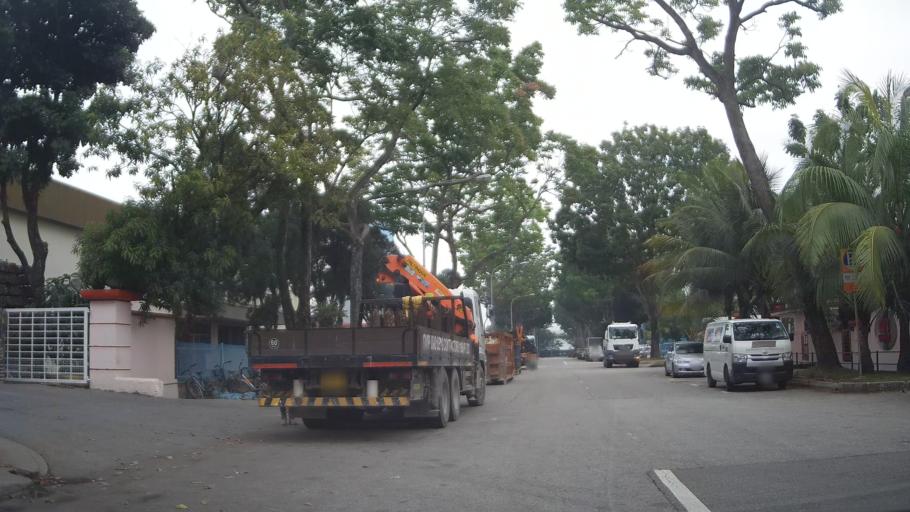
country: MY
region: Johor
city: Johor Bahru
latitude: 1.3175
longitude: 103.6738
